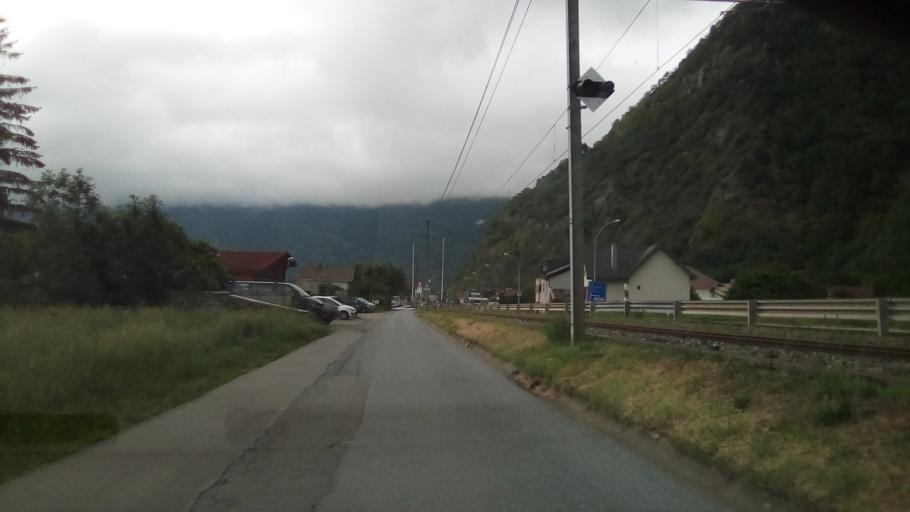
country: CH
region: Valais
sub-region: Martigny District
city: Martigny-Ville
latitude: 46.1111
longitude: 7.0630
